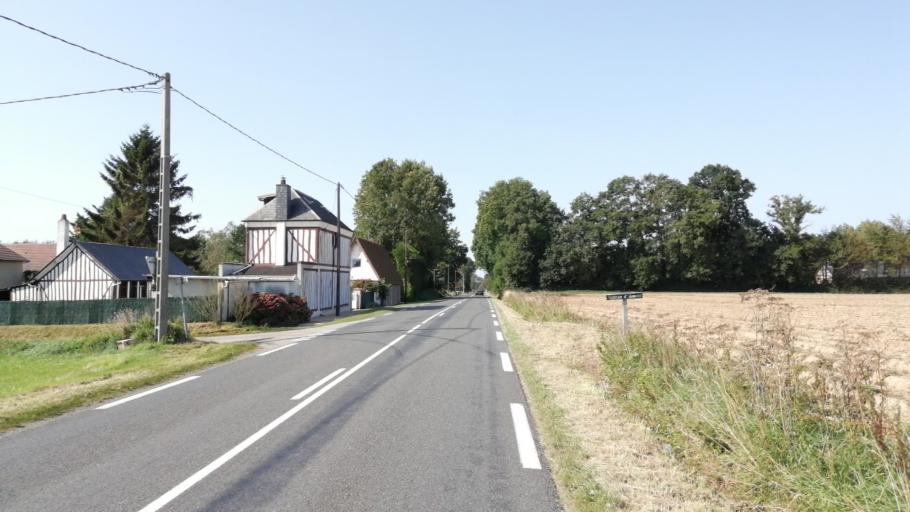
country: FR
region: Haute-Normandie
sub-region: Departement de la Seine-Maritime
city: Saint-Romain-de-Colbosc
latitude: 49.5254
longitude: 0.3787
